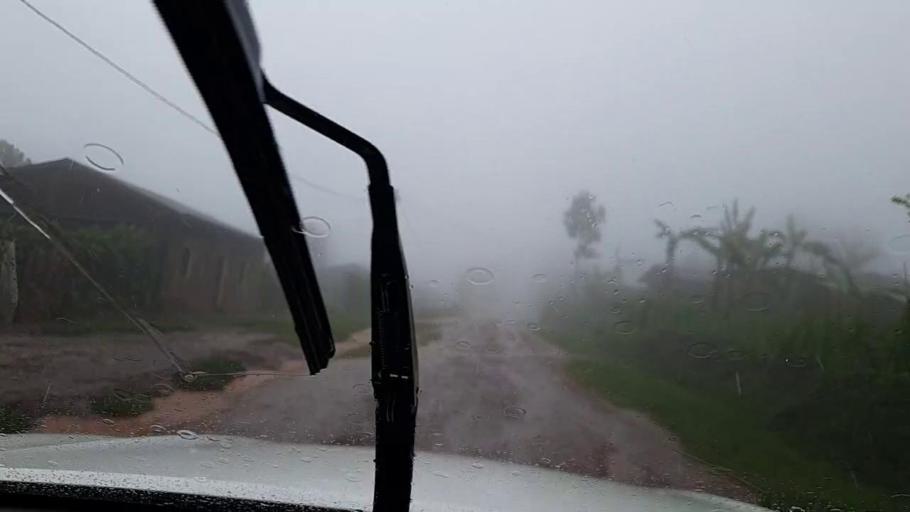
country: RW
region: Northern Province
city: Byumba
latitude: -1.7319
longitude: 30.0156
